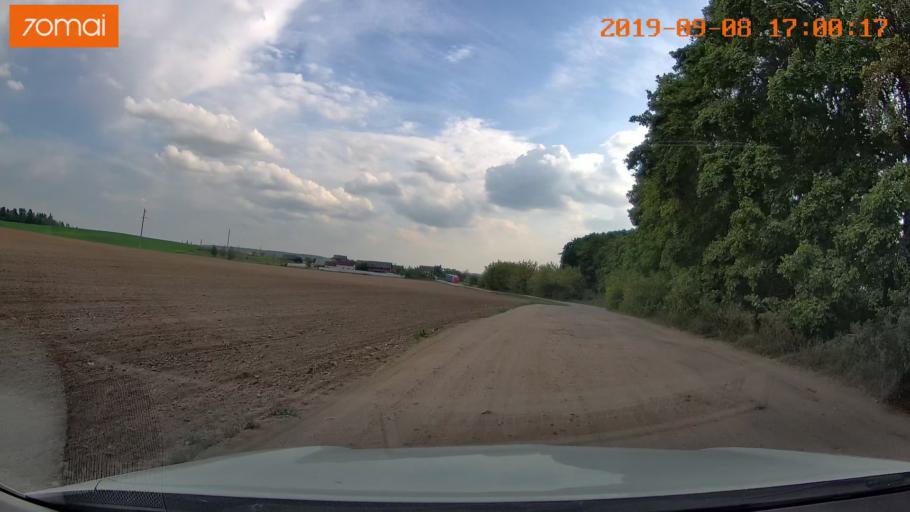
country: BY
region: Grodnenskaya
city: Hrodna
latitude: 53.7166
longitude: 23.9324
